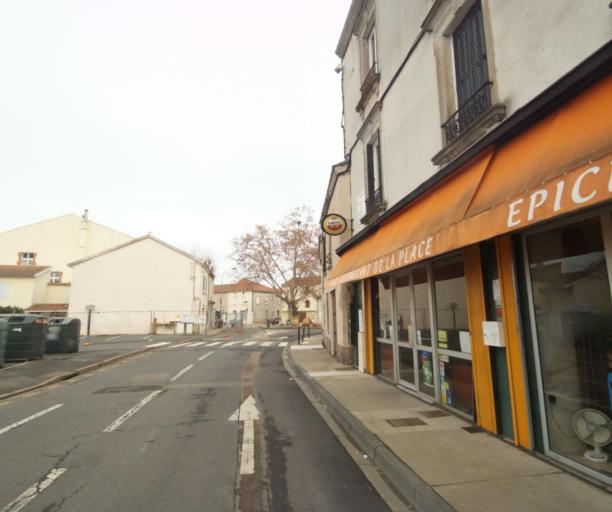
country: FR
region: Rhone-Alpes
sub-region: Departement de la Loire
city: Roanne
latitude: 46.0283
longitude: 4.0672
